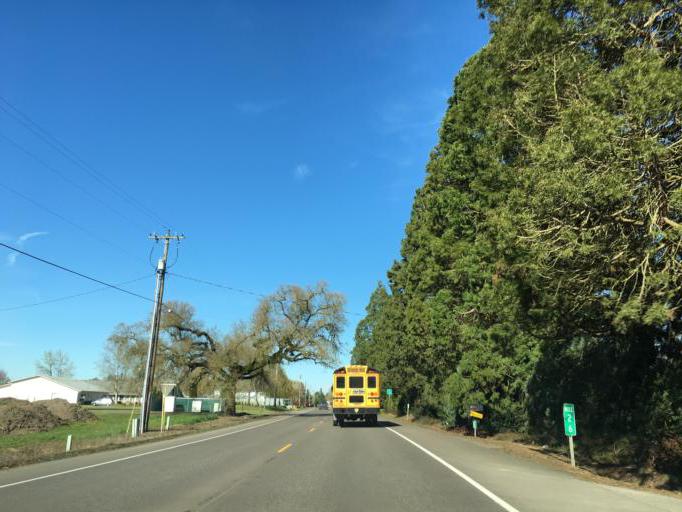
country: US
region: Oregon
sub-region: Marion County
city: Hubbard
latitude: 45.2182
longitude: -122.7632
